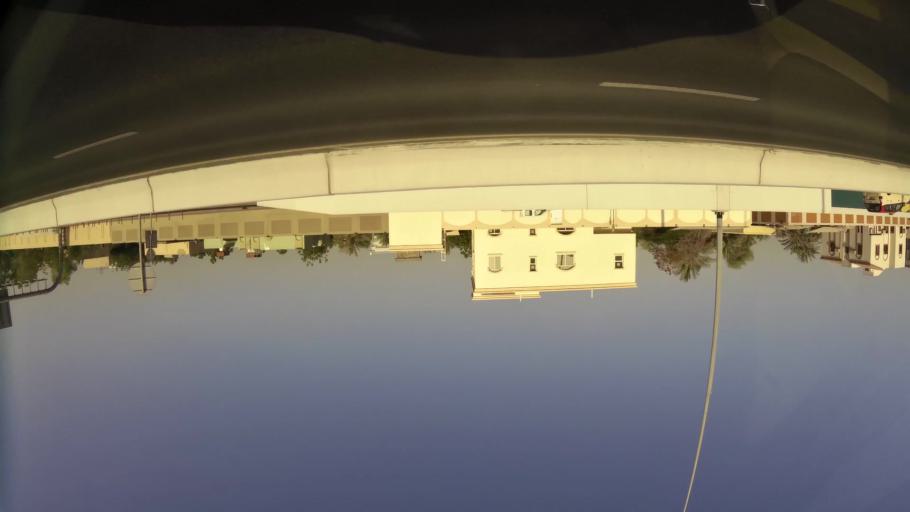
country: AE
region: Ash Shariqah
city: Sharjah
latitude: 25.2584
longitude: 55.3879
